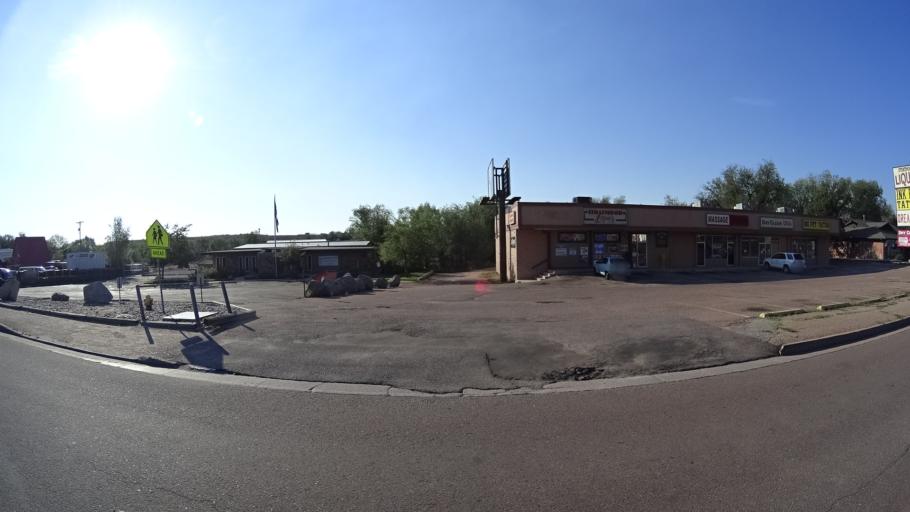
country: US
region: Colorado
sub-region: El Paso County
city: Stratmoor
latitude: 38.7746
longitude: -104.7919
